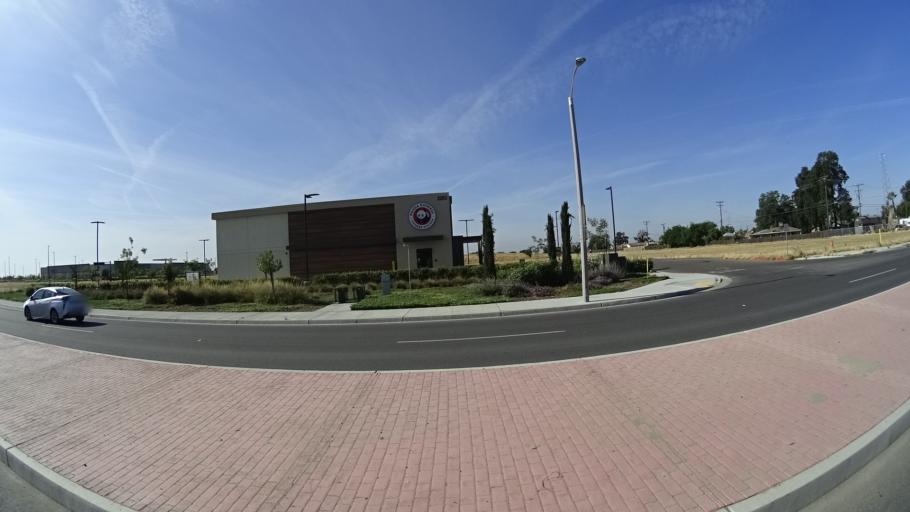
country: US
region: California
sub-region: Kings County
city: Hanford
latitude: 36.3280
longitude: -119.6092
